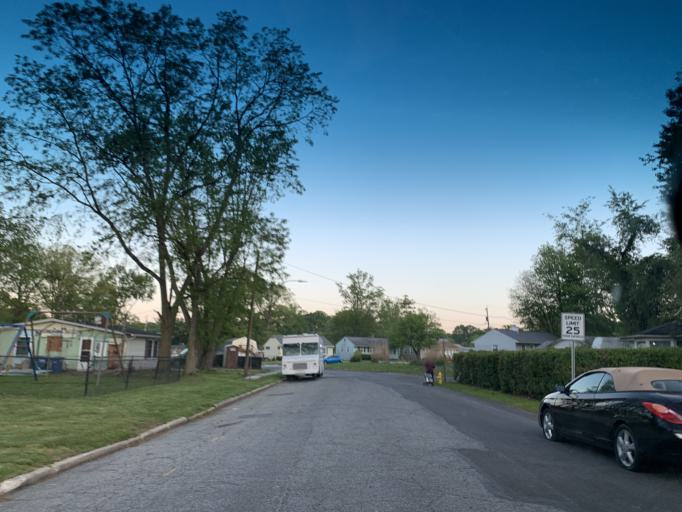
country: US
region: Maryland
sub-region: Harford County
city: Aberdeen
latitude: 39.5044
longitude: -76.1758
